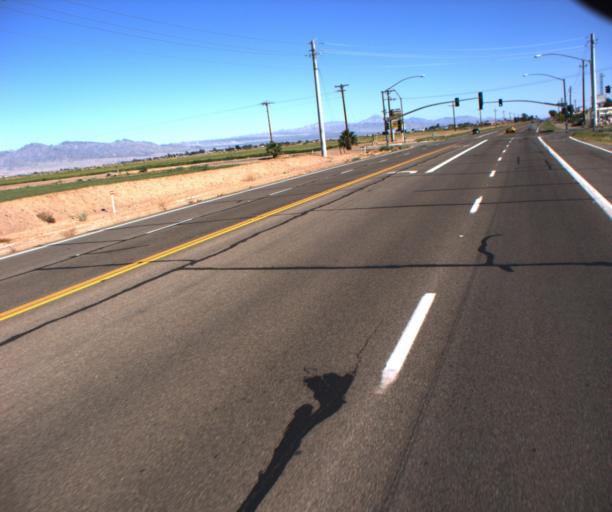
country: US
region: Arizona
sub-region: Mohave County
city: Willow Valley
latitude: 34.8942
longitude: -114.5978
